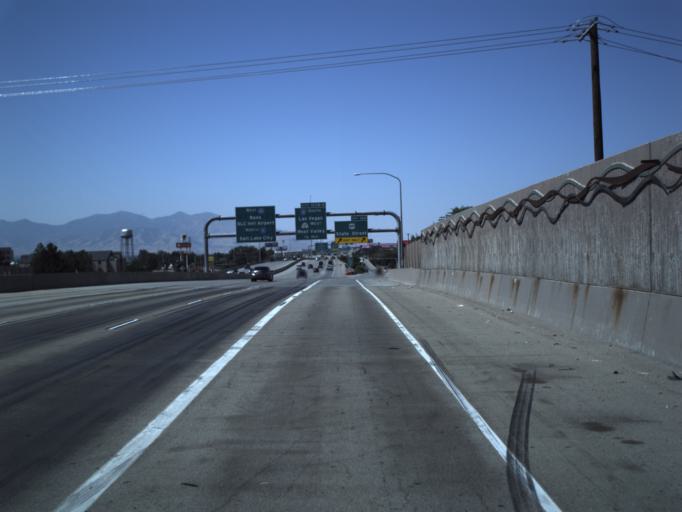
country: US
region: Utah
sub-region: Salt Lake County
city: South Salt Lake
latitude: 40.7184
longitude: -111.8822
